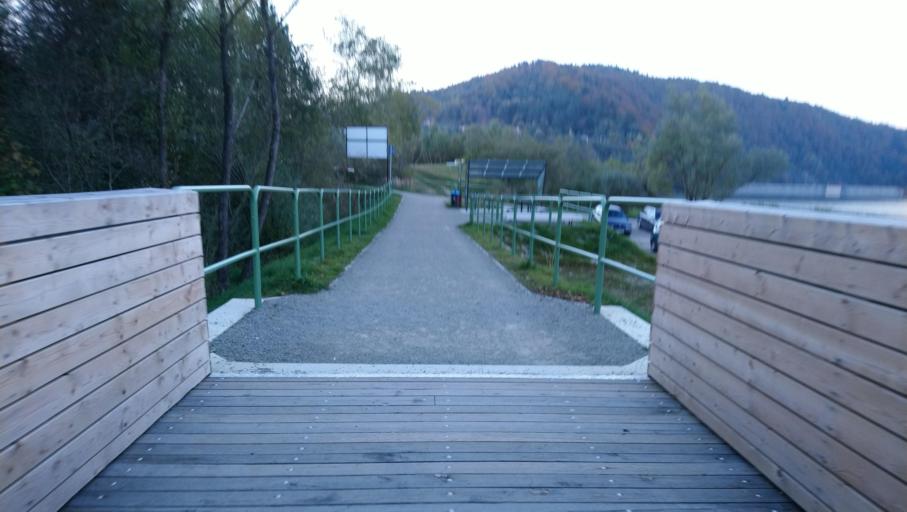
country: PL
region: Lesser Poland Voivodeship
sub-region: Powiat gorlicki
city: Ropa
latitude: 49.5521
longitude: 21.0817
